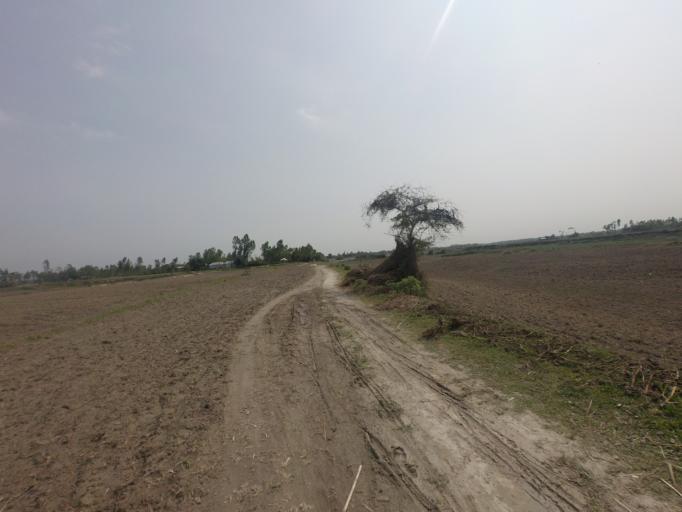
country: BD
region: Rajshahi
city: Sirajganj
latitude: 24.3502
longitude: 89.7277
